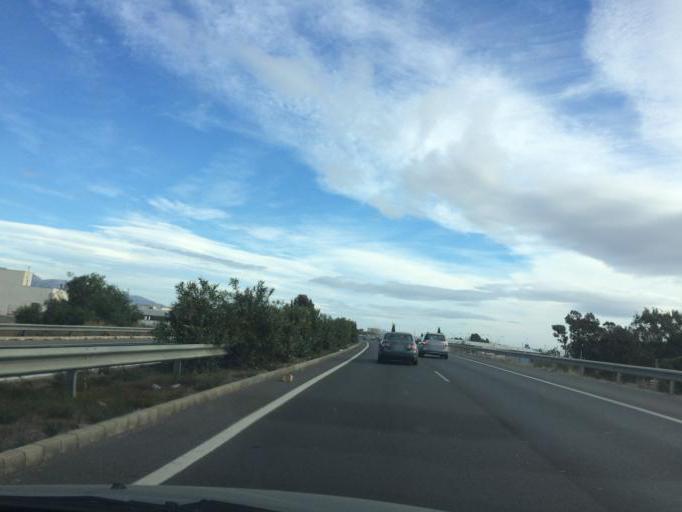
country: ES
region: Andalusia
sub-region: Provincia de Almeria
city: Viator
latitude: 36.8455
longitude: -2.3924
